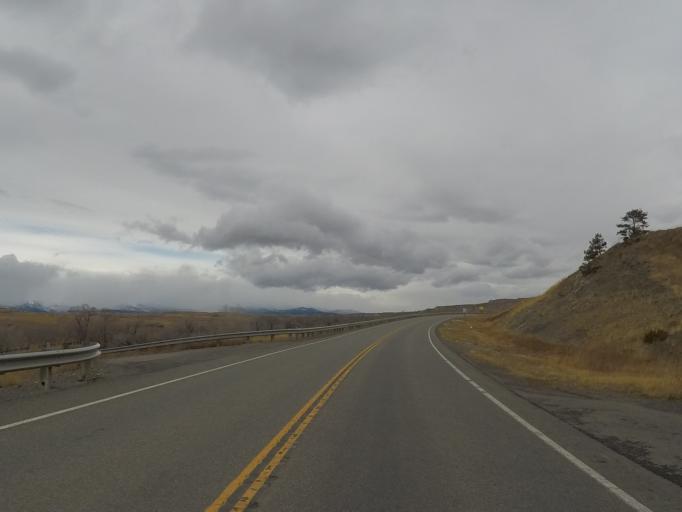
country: US
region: Montana
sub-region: Sweet Grass County
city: Big Timber
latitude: 45.8810
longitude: -109.9559
